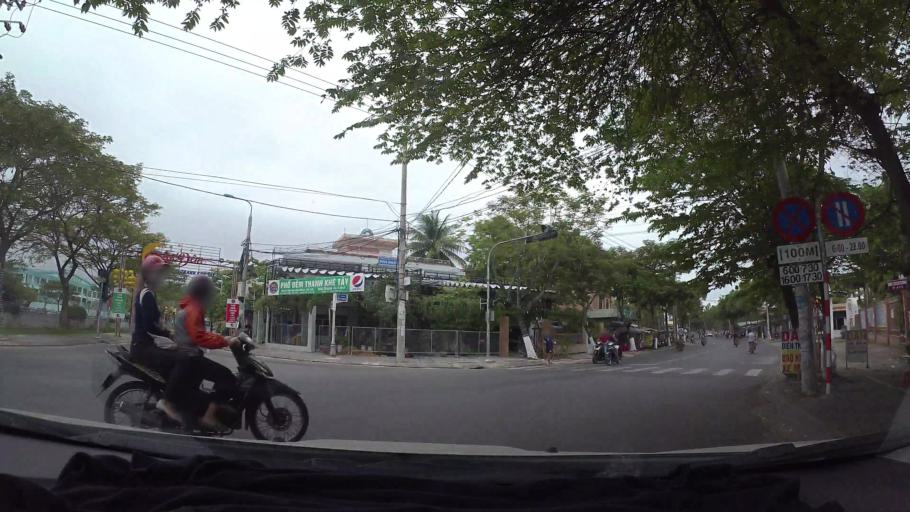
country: VN
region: Da Nang
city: Thanh Khe
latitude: 16.0694
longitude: 108.1811
